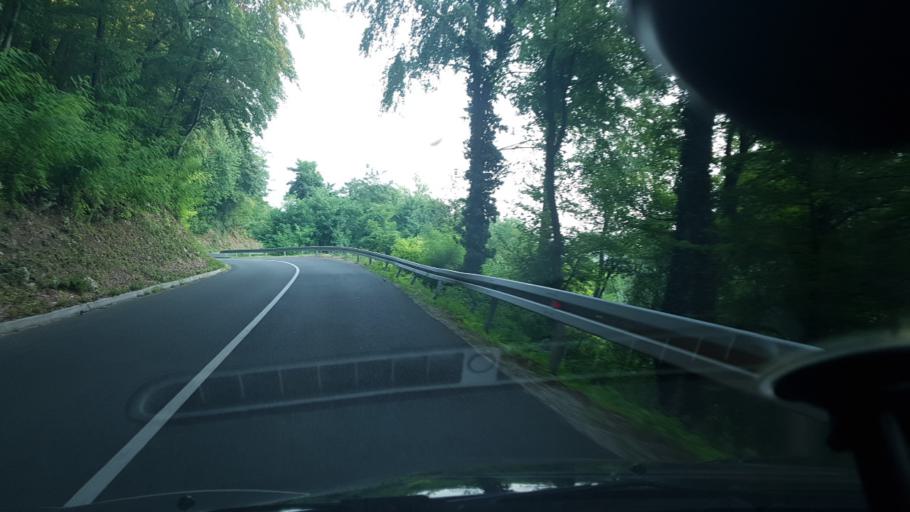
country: HR
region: Krapinsko-Zagorska
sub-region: Grad Krapina
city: Krapina
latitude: 46.1682
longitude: 15.8503
